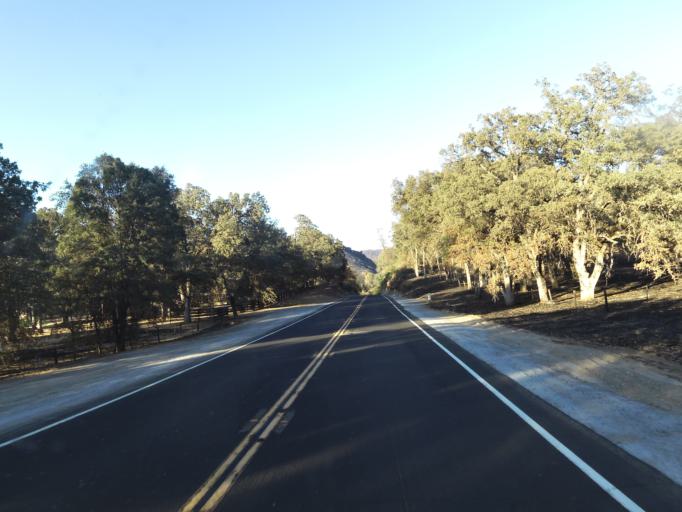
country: US
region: California
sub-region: Mariposa County
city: Mariposa
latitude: 37.4769
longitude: -120.0354
